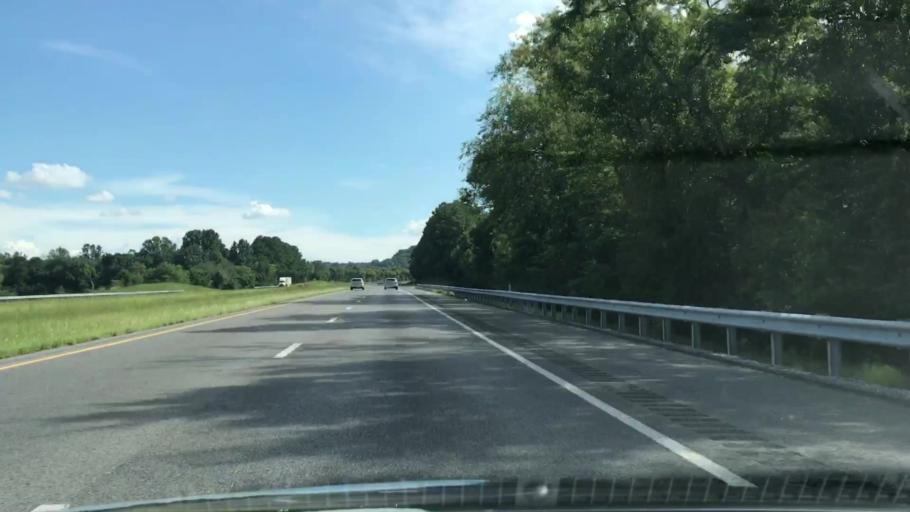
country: US
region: Tennessee
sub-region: Marshall County
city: Cornersville
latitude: 35.4213
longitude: -86.8781
